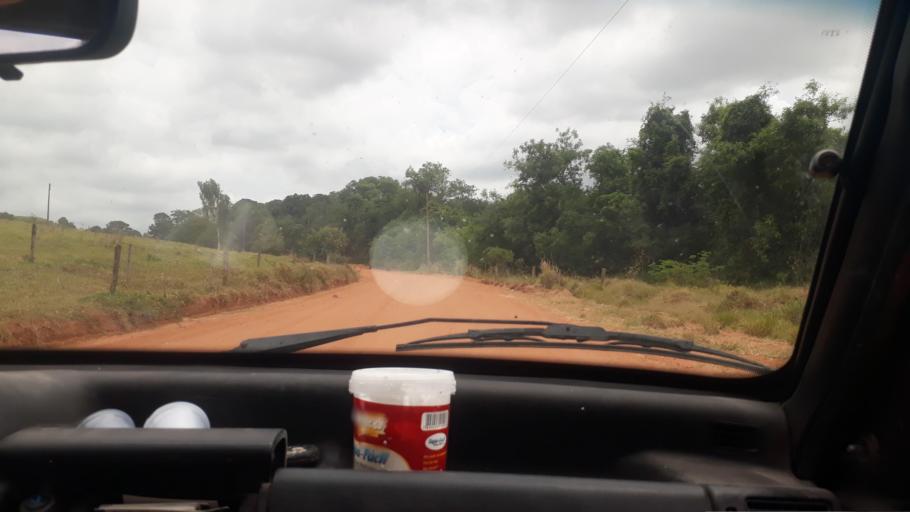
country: BR
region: Sao Paulo
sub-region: Regente Feijo
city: Regente Feijo
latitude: -22.2390
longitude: -51.2978
